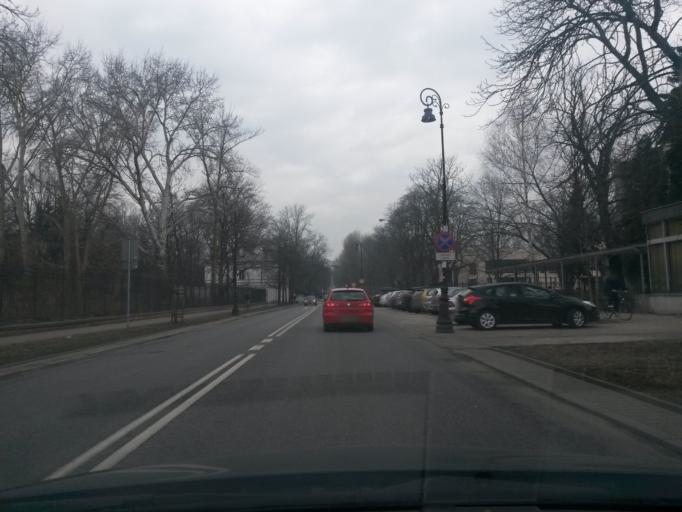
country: PL
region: Masovian Voivodeship
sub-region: Warszawa
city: Mokotow
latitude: 52.2168
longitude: 21.0399
